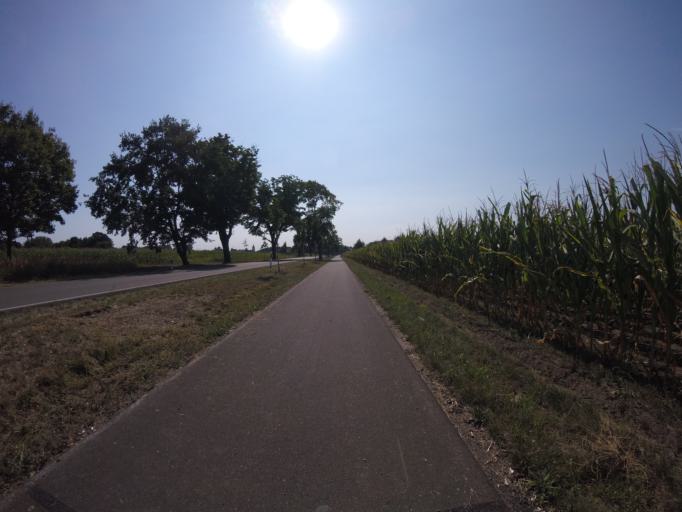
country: DE
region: Brandenburg
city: Mullrose
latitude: 52.2490
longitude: 14.4016
